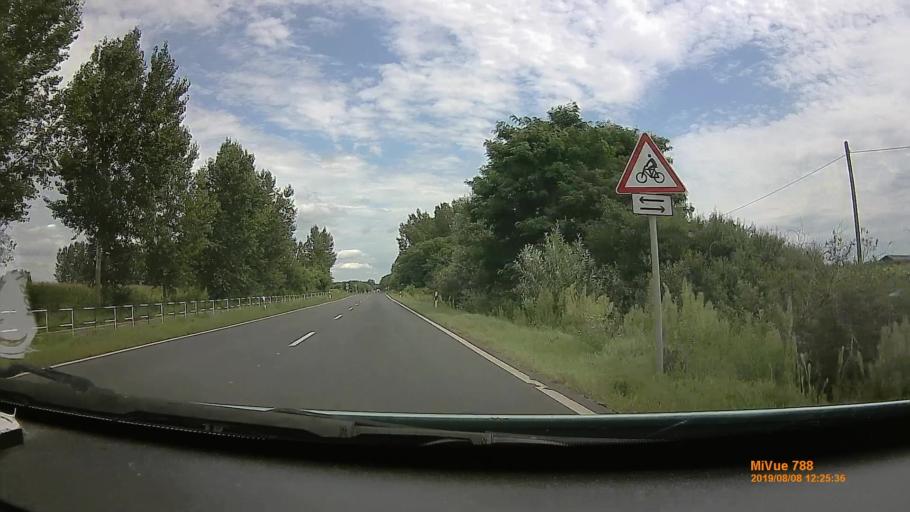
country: HU
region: Szabolcs-Szatmar-Bereg
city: Nyirbogat
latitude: 47.8117
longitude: 22.0737
